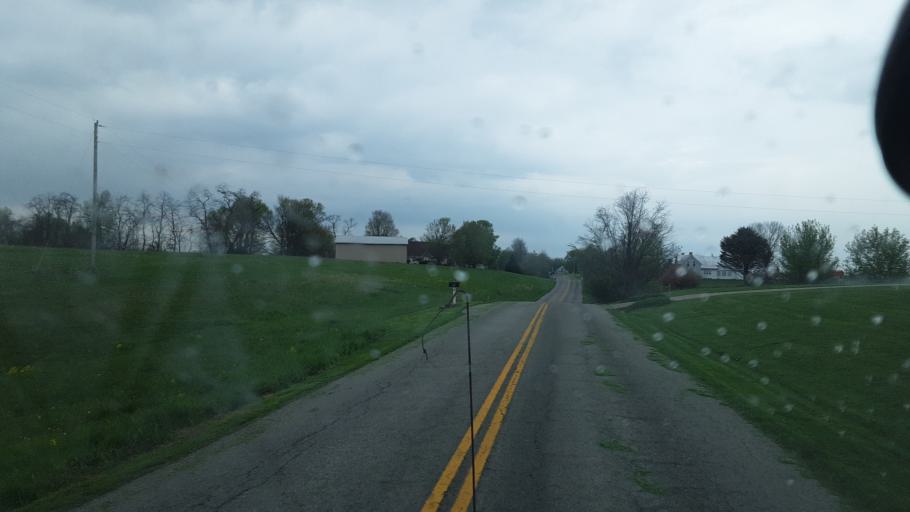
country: US
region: Kentucky
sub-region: Owen County
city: Owenton
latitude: 38.6320
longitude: -84.7786
